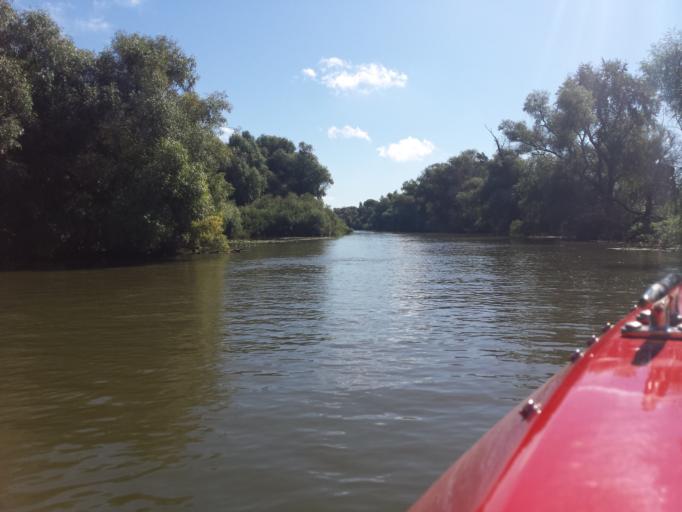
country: RO
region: Tulcea
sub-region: Comuna Mahmudia
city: Mahmudia
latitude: 45.2149
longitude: 29.1817
